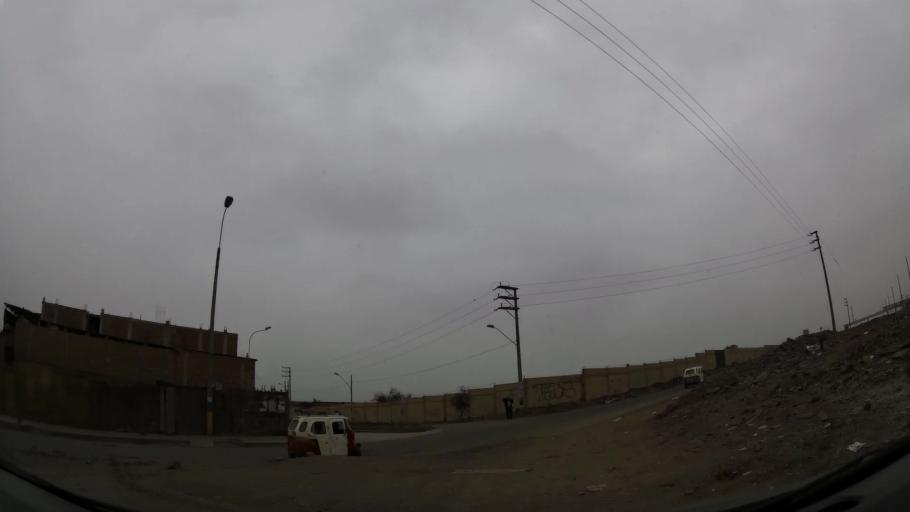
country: PE
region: Lima
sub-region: Lima
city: Surco
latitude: -12.2155
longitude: -76.9287
